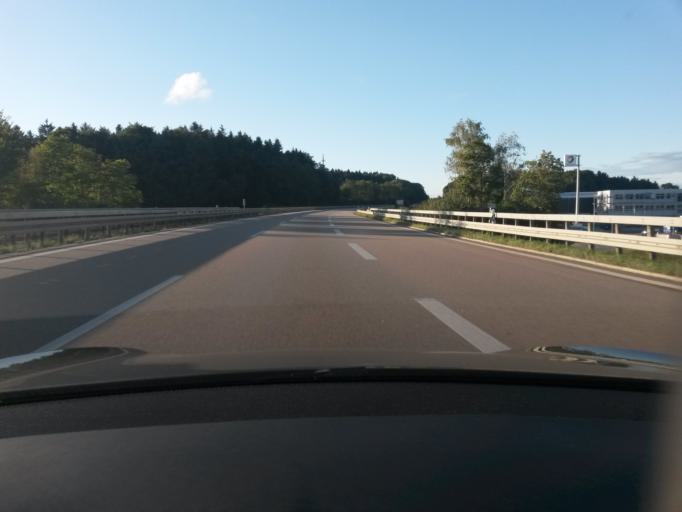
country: DE
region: Bavaria
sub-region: Upper Palatinate
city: Brunn
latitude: 49.0901
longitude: 11.8879
